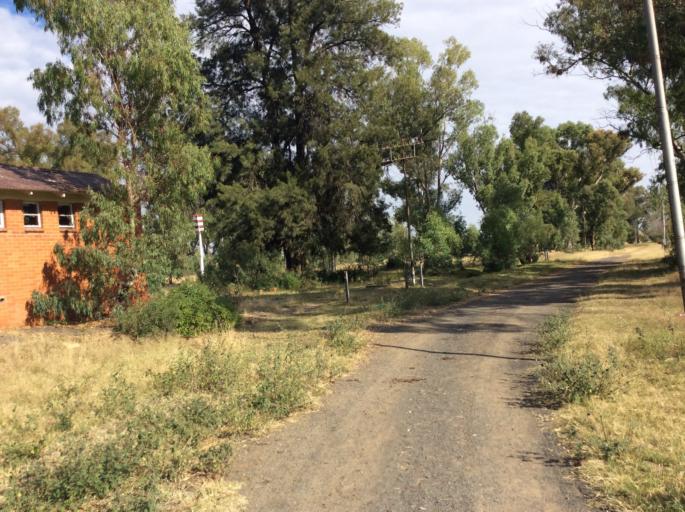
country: LS
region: Mafeteng
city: Mafeteng
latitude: -29.7313
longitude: 27.0269
